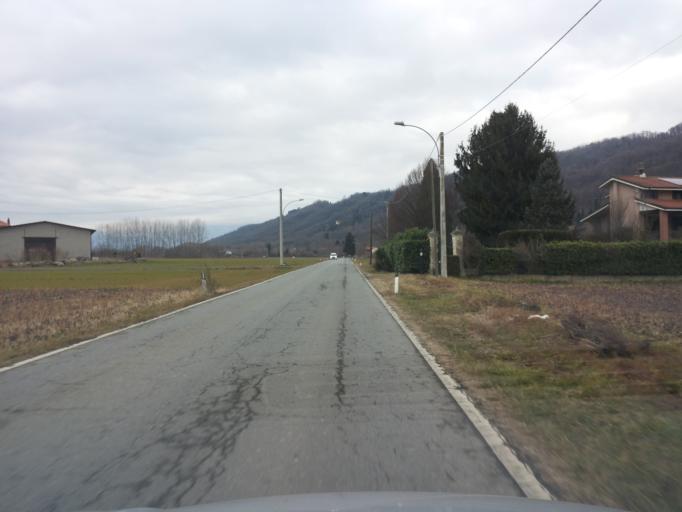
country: IT
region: Piedmont
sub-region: Provincia di Torino
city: Borgomasino
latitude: 45.3706
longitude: 7.9807
